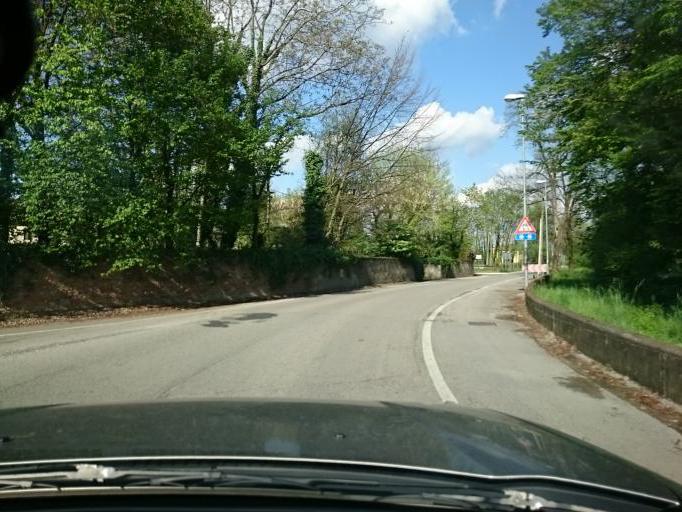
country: IT
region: Veneto
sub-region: Provincia di Treviso
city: Badoere
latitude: 45.6259
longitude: 12.0561
